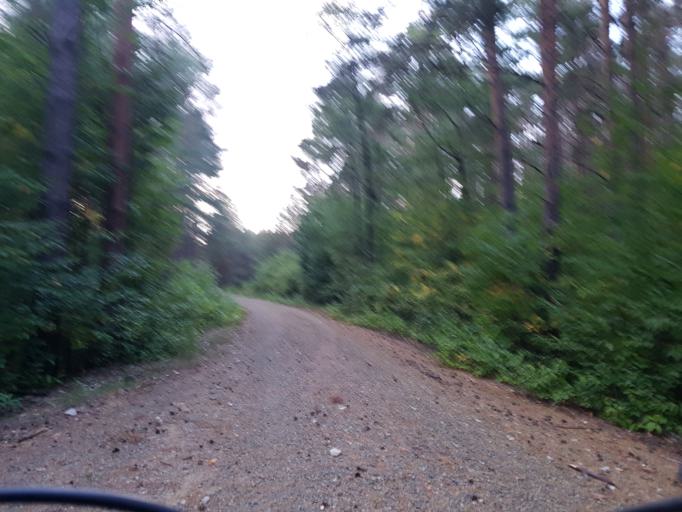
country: DE
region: Brandenburg
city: Trobitz
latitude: 51.5635
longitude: 13.4507
